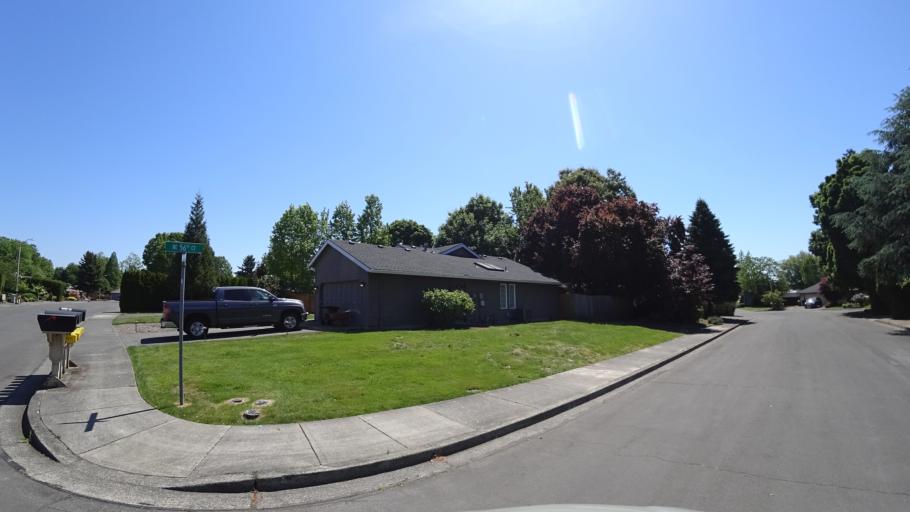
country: US
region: Oregon
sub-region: Washington County
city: Rockcreek
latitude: 45.5349
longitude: -122.9254
